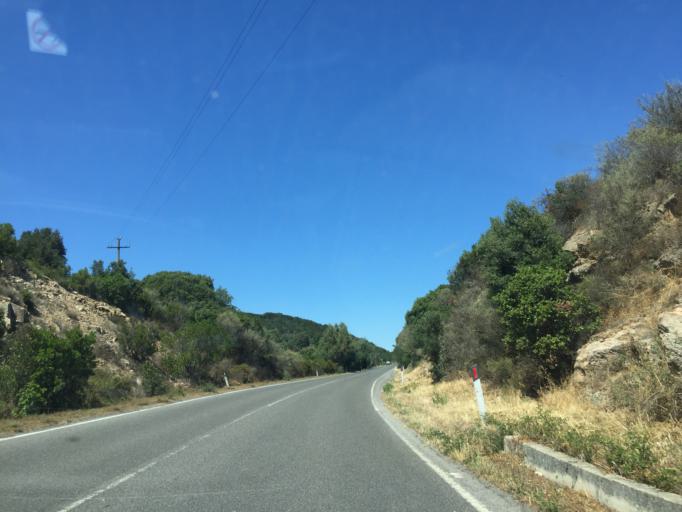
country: IT
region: Sardinia
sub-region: Provincia di Olbia-Tempio
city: Aglientu
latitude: 41.0776
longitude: 9.1161
